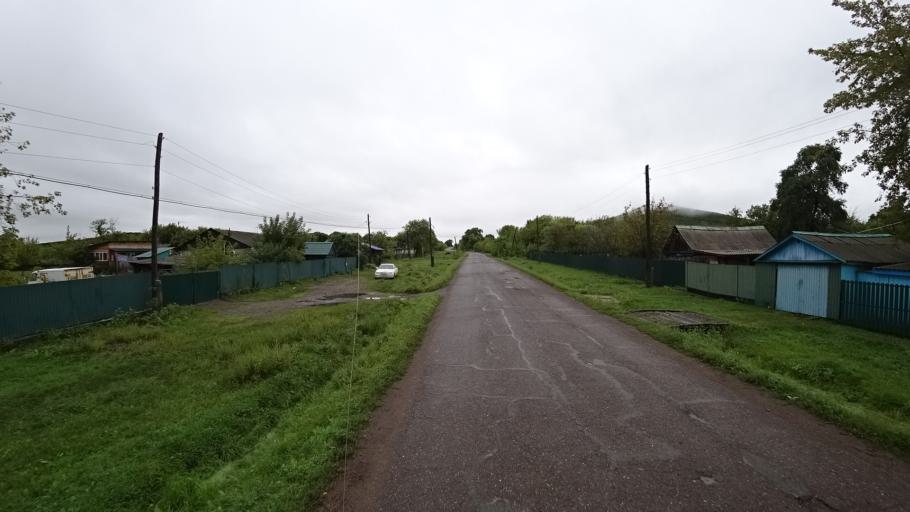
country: RU
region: Primorskiy
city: Monastyrishche
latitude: 44.2562
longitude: 132.4259
